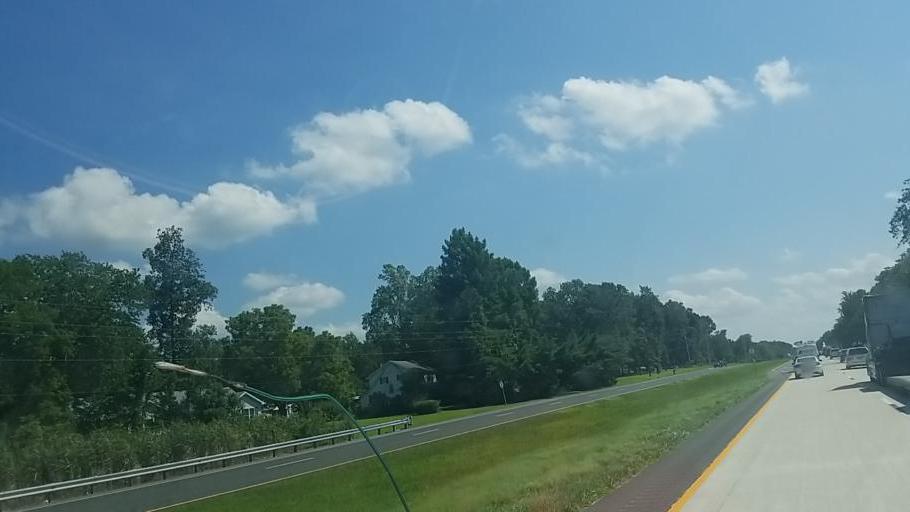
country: US
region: Delaware
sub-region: Sussex County
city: Milford
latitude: 38.8367
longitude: -75.4391
